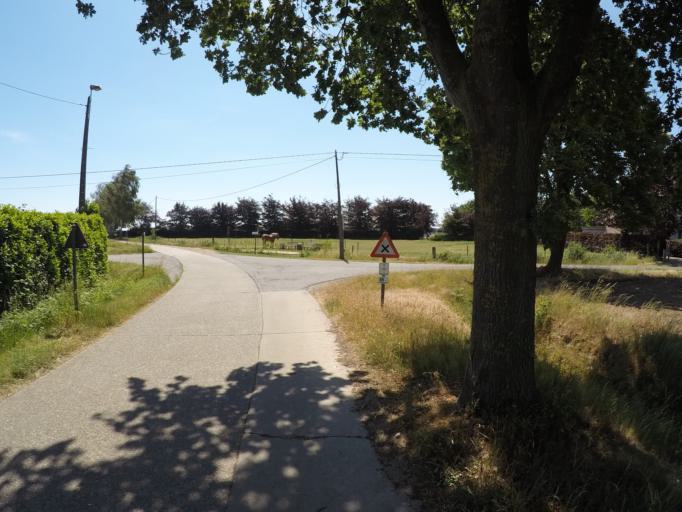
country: BE
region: Flanders
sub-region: Provincie Antwerpen
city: Brecht
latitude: 51.3810
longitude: 4.6893
